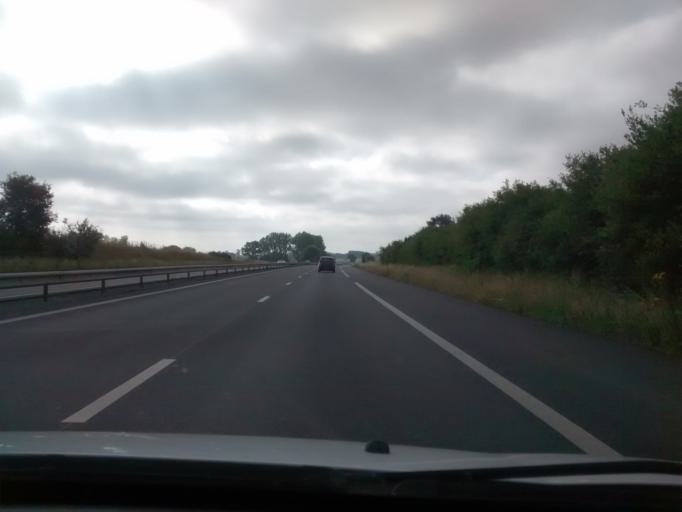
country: FR
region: Brittany
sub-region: Departement d'Ille-et-Vilaine
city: Saint-Didier
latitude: 48.0865
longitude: -1.3508
